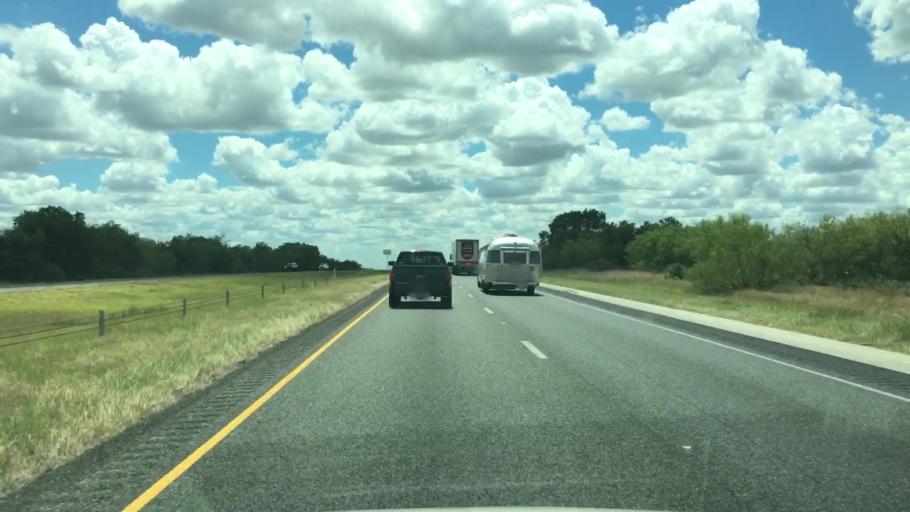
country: US
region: Texas
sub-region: Bexar County
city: Elmendorf
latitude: 29.1290
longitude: -98.4305
